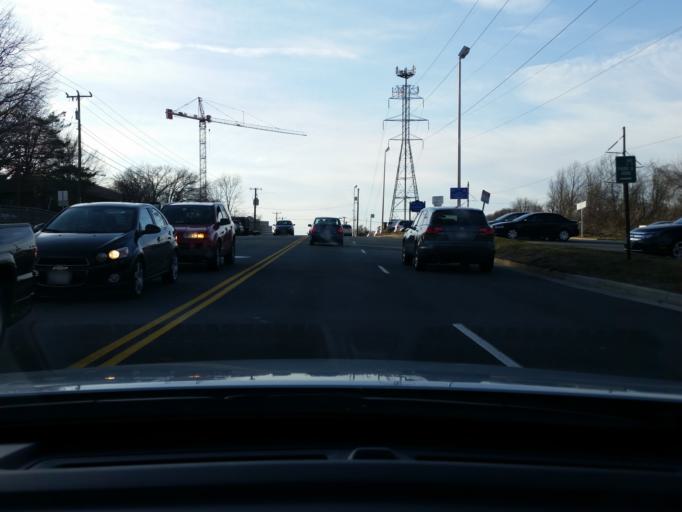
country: US
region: Virginia
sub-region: Fairfax County
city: Reston
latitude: 38.9502
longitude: -77.3365
